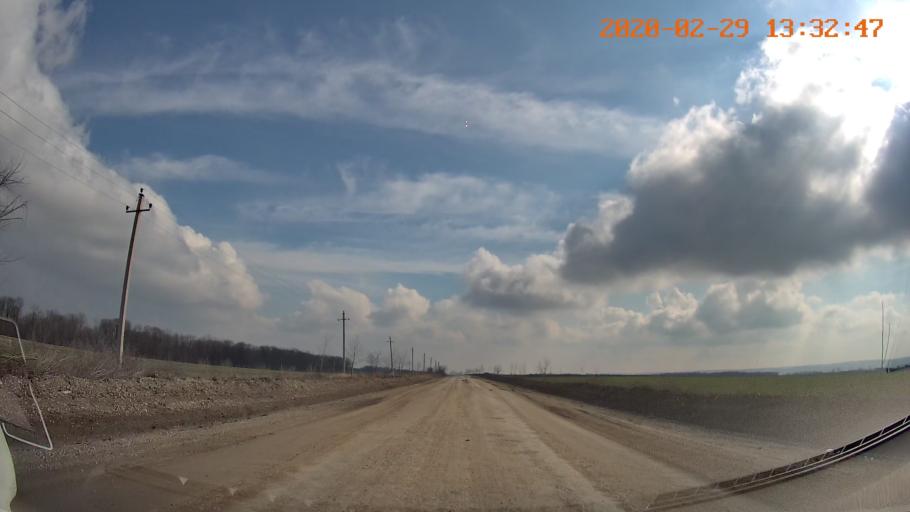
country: MD
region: Telenesti
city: Camenca
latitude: 47.8772
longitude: 28.6120
